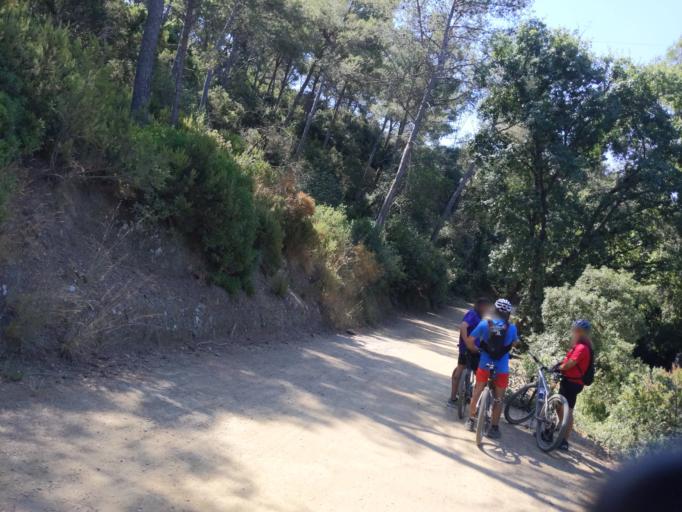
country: ES
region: Catalonia
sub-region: Provincia de Barcelona
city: Nou Barris
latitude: 41.4534
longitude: 2.1534
